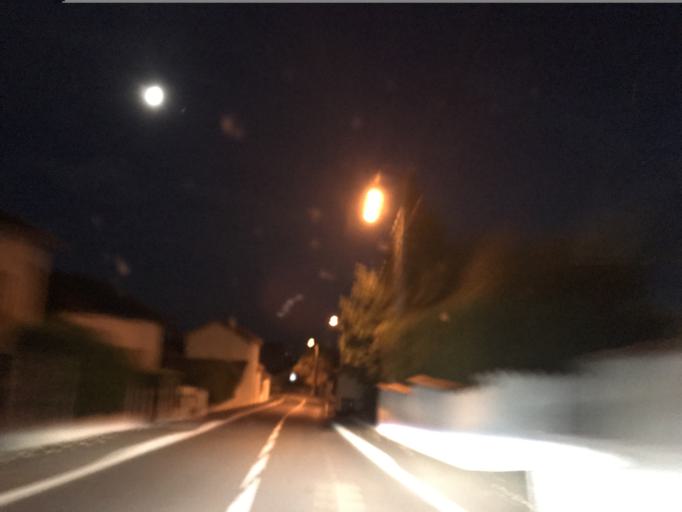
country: FR
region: Auvergne
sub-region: Departement du Puy-de-Dome
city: Thiers
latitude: 45.8624
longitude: 3.5310
